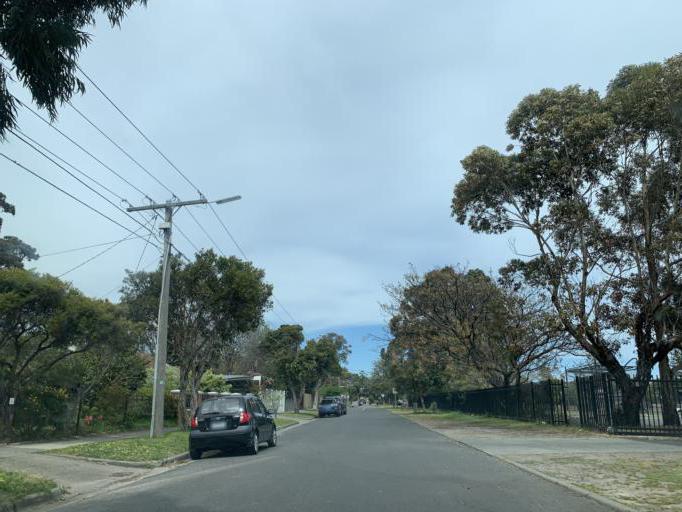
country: AU
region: Victoria
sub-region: Bayside
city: Hampton East
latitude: -37.9512
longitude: 145.0236
